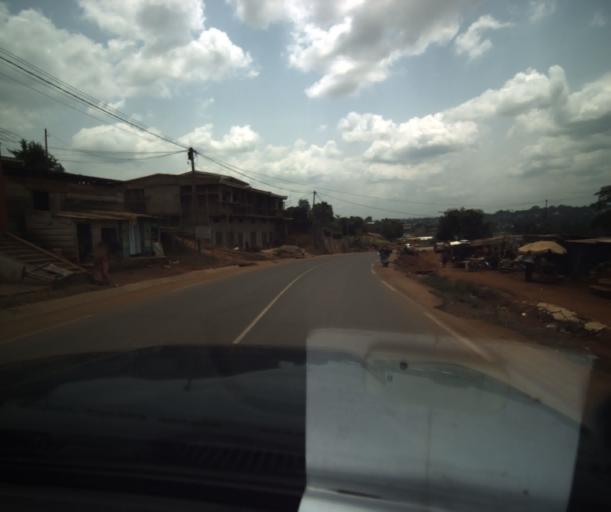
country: CM
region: Centre
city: Yaounde
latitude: 3.8192
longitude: 11.4715
